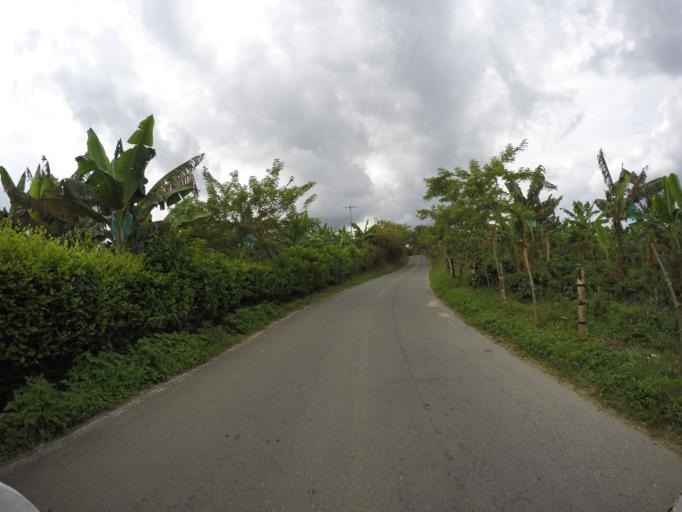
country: CO
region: Quindio
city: Quimbaya
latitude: 4.6068
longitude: -75.7274
